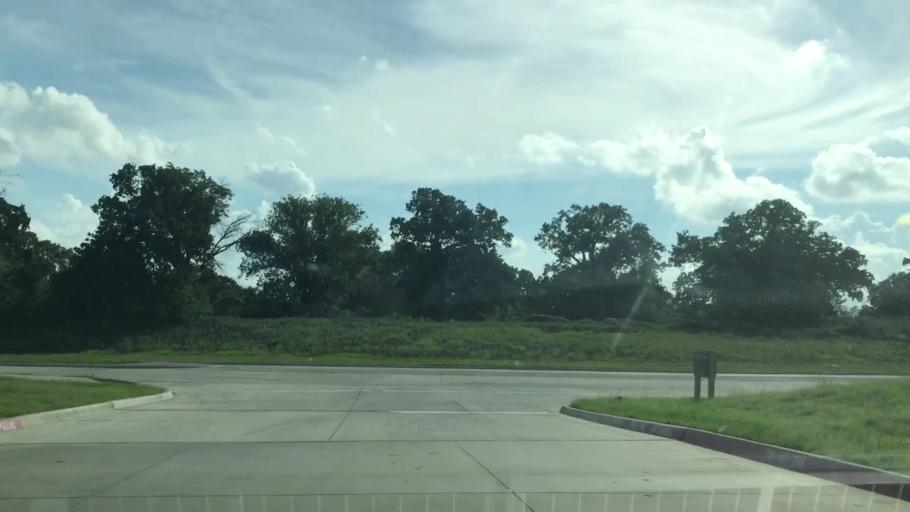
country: US
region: Texas
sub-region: Dallas County
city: Coppell
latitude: 32.9787
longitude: -97.0284
